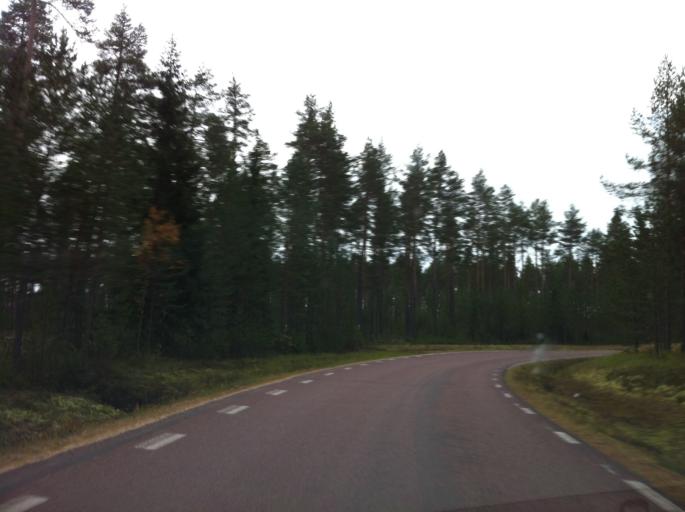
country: SE
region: Dalarna
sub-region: Mora Kommun
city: Mora
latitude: 61.1039
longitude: 14.4519
